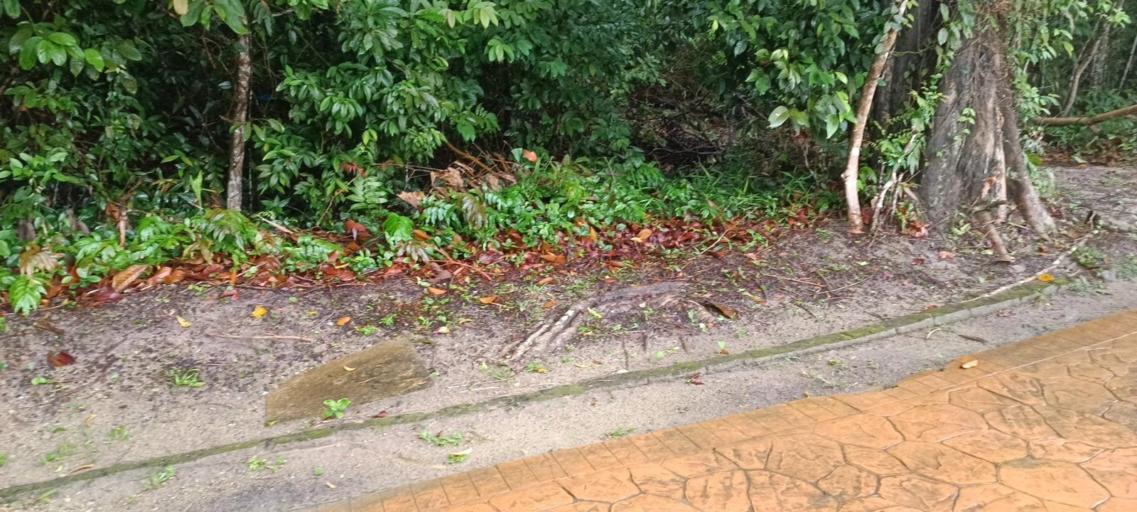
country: MY
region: Penang
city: Tanjung Tokong
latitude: 5.4615
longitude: 100.2046
